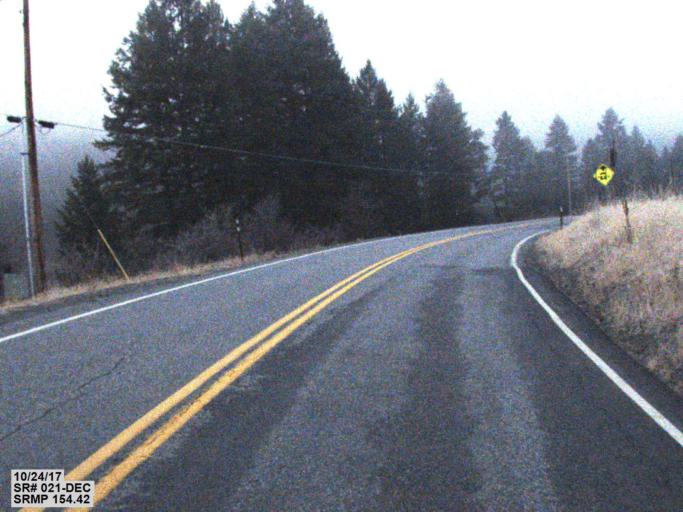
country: US
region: Washington
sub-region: Ferry County
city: Republic
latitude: 48.5628
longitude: -118.7438
